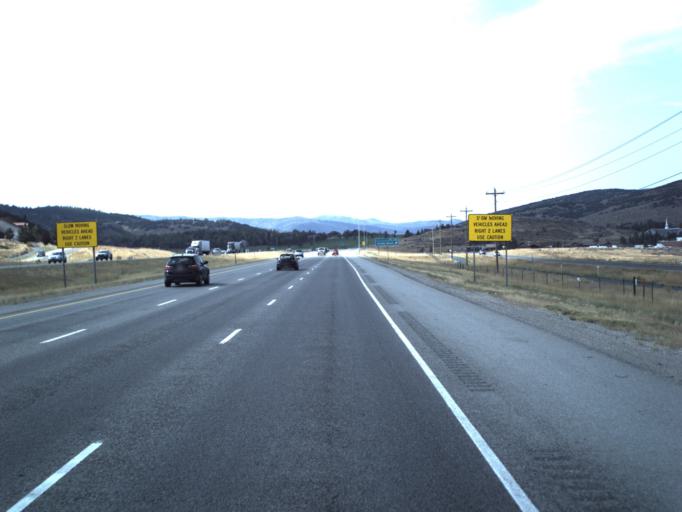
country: US
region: Utah
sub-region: Summit County
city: Summit Park
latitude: 40.7484
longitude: -111.5661
